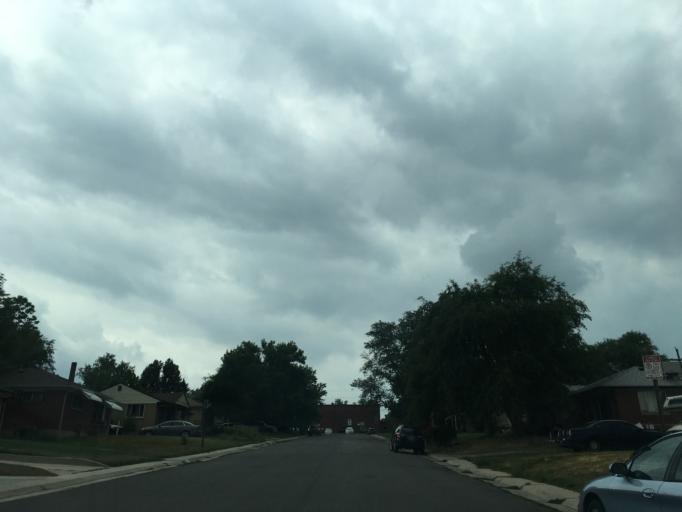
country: US
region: Colorado
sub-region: Arapahoe County
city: Sheridan
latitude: 39.6872
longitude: -105.0196
